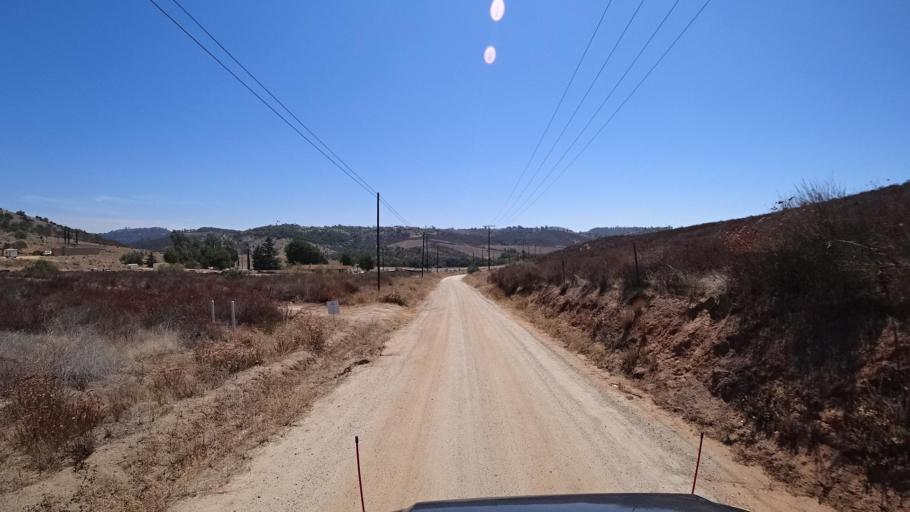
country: US
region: California
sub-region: San Diego County
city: Hidden Meadows
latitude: 33.2937
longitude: -117.0818
